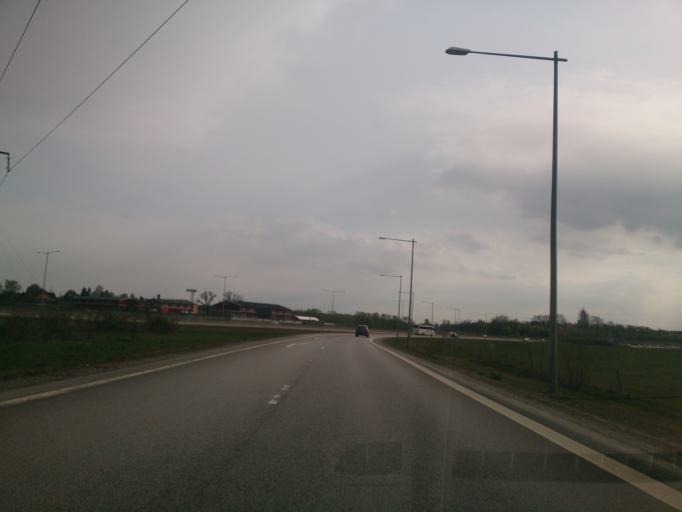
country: SE
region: OEstergoetland
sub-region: Norrkopings Kommun
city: Norrkoping
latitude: 58.5794
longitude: 16.1056
